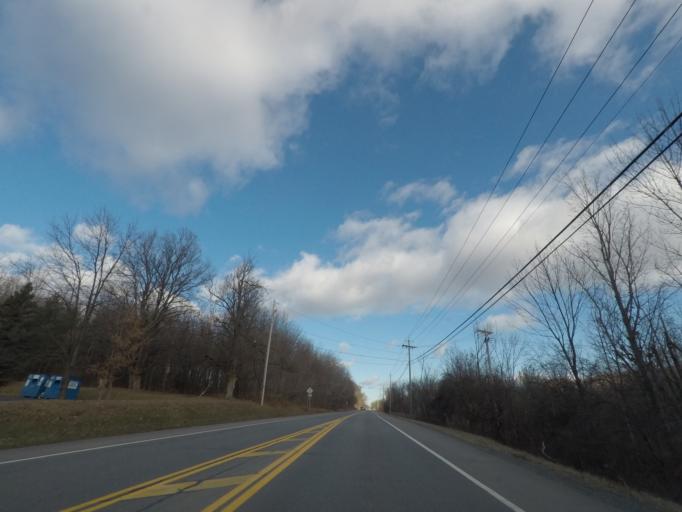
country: US
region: New York
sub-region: Saratoga County
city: Waterford
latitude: 42.7664
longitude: -73.6612
